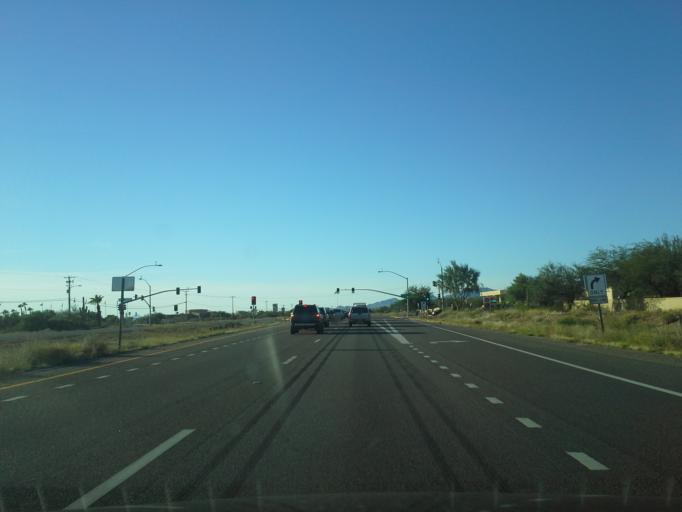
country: US
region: Arizona
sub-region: Pinal County
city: Apache Junction
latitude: 33.3569
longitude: -111.4661
